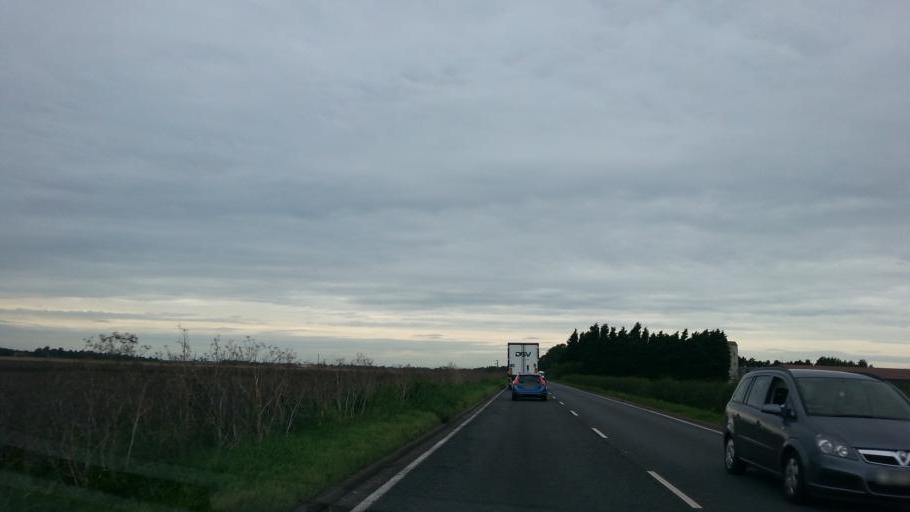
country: GB
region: England
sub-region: Peterborough
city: Thorney
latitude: 52.6176
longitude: -0.0279
